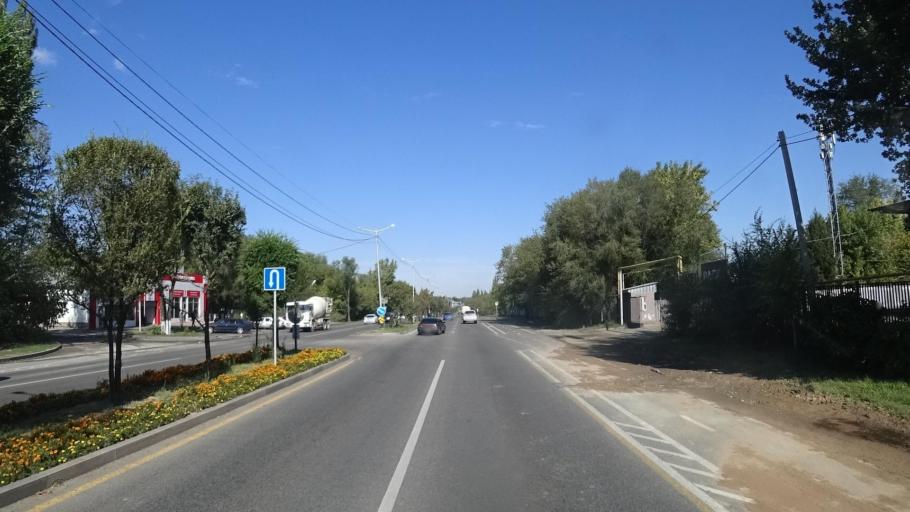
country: KZ
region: Almaty Oblysy
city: Pervomayskiy
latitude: 43.3375
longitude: 77.0012
